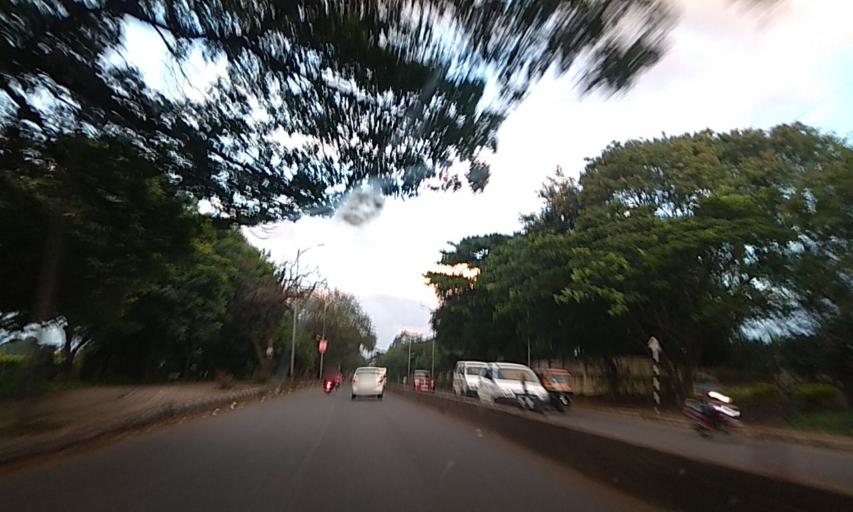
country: IN
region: Maharashtra
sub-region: Pune Division
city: Pune
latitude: 18.5067
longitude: 73.8916
